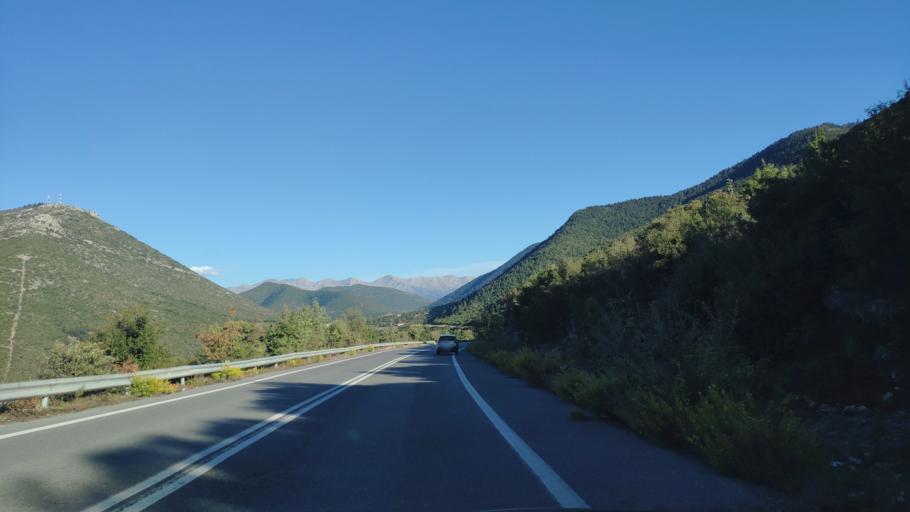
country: GR
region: Peloponnese
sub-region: Nomos Arkadias
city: Langadhia
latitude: 37.7274
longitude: 22.2073
